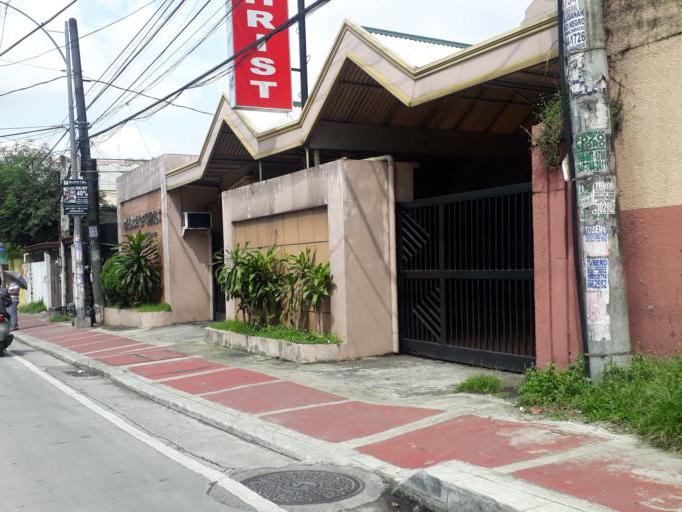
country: PH
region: Metro Manila
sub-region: San Juan
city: San Juan
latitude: 14.6157
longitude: 121.0503
